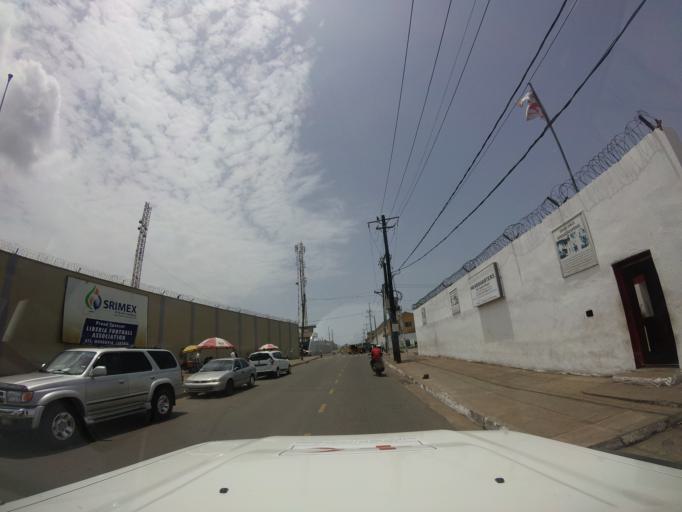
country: LR
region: Montserrado
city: Monrovia
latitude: 6.3094
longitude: -10.8050
